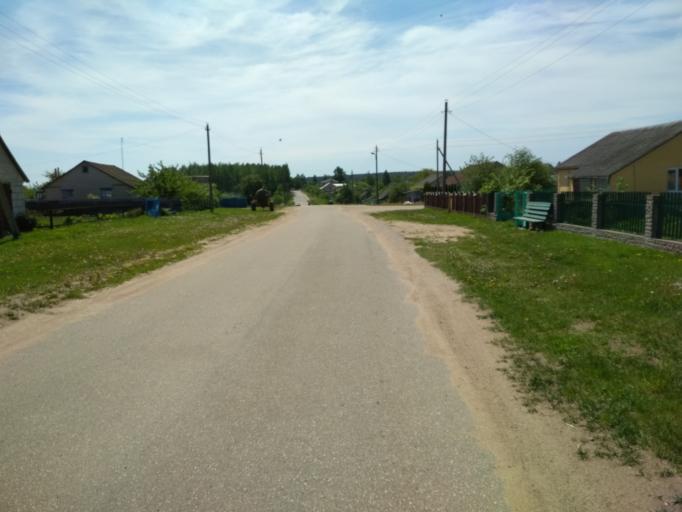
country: BY
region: Grodnenskaya
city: Mir
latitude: 53.3853
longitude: 26.3622
